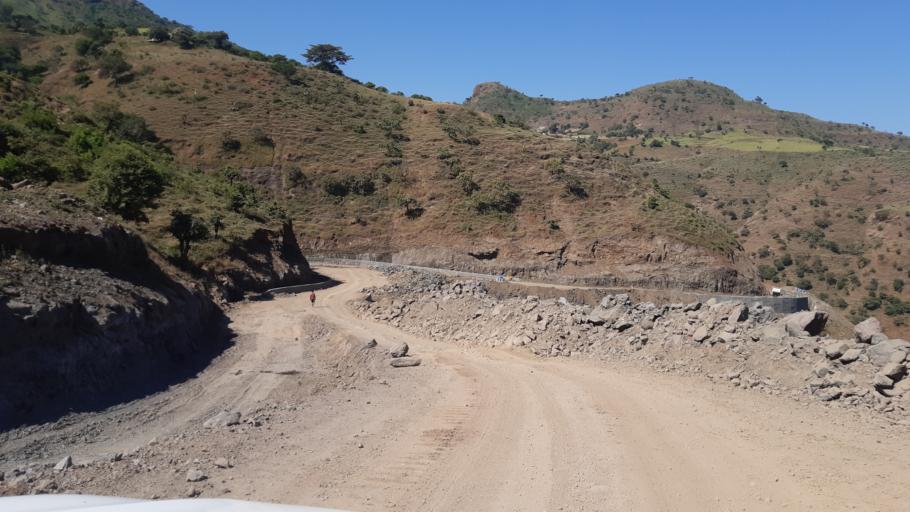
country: ET
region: Amhara
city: Dabat
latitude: 13.1674
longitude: 37.6038
